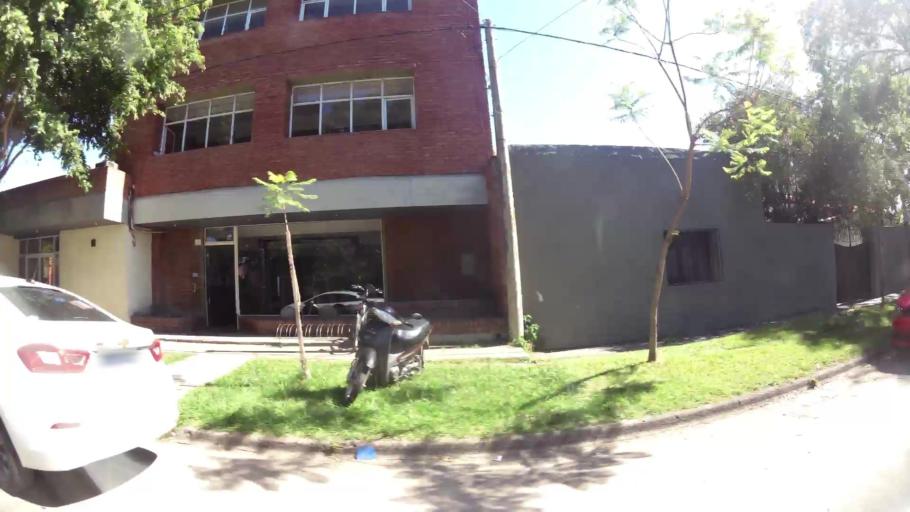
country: AR
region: Santa Fe
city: Santa Fe de la Vera Cruz
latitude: -31.6008
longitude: -60.6676
